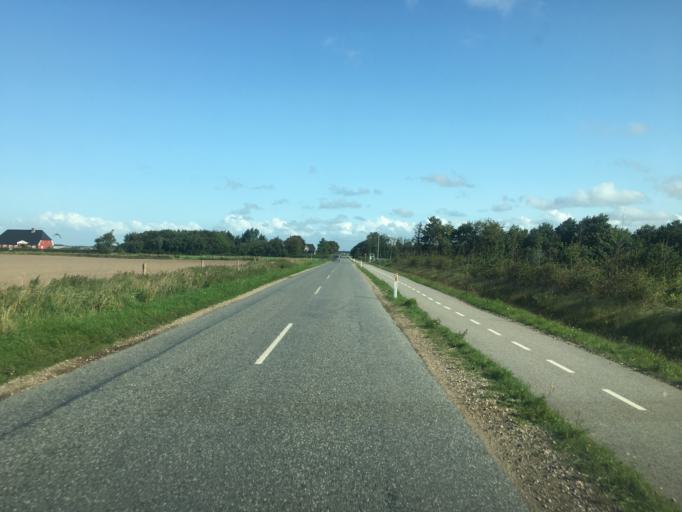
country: DK
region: South Denmark
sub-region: Tonder Kommune
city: Sherrebek
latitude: 55.1305
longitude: 8.7612
